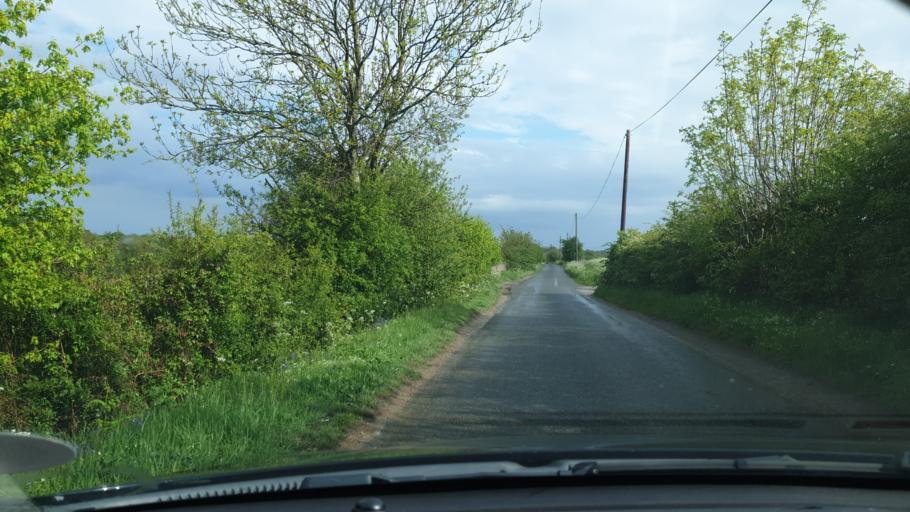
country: GB
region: England
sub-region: Essex
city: Great Bentley
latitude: 51.8383
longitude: 1.0517
